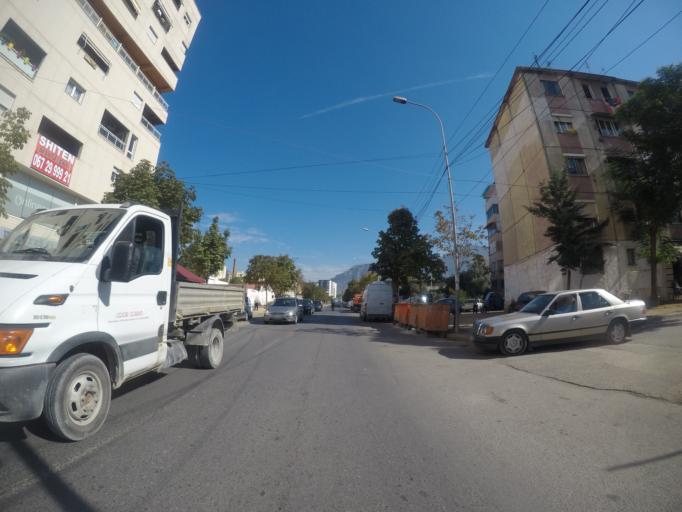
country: AL
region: Tirane
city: Tirana
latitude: 41.3400
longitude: 19.8436
